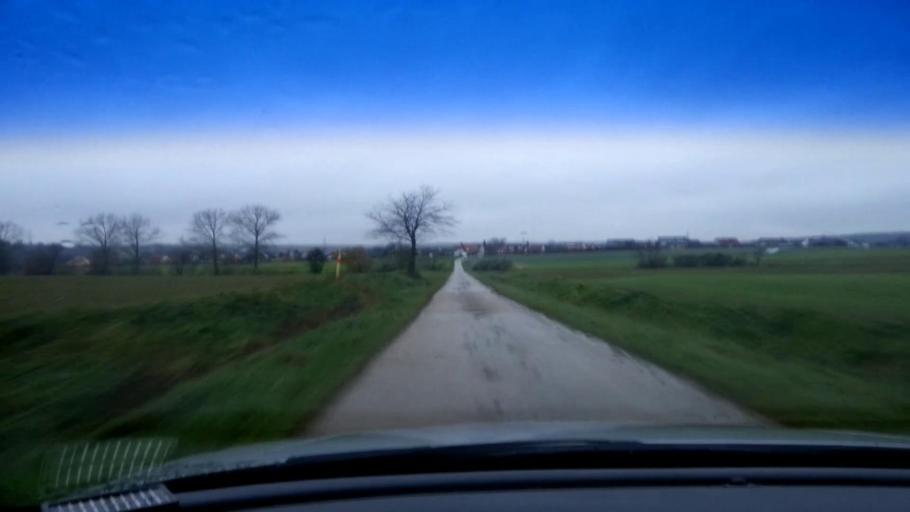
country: DE
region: Bavaria
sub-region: Upper Franconia
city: Schesslitz
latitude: 49.9535
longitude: 11.0047
